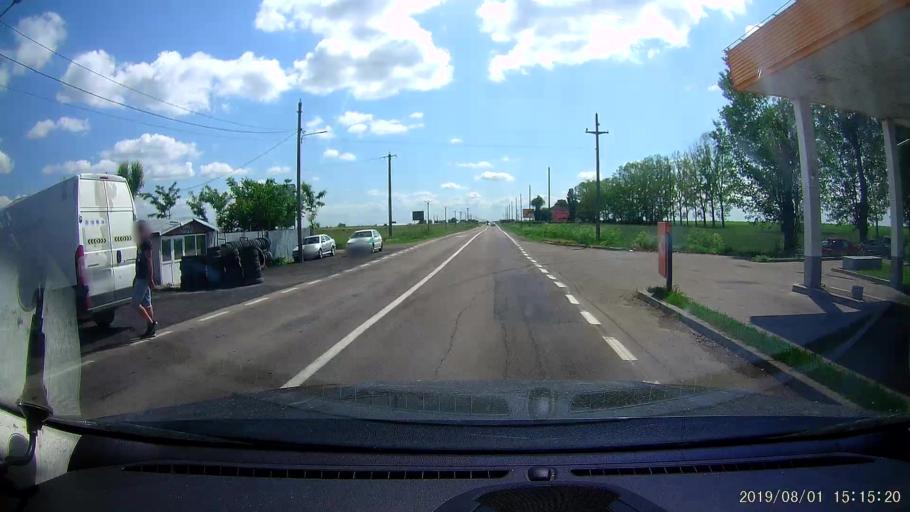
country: RO
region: Braila
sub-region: Comuna Chiscani
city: Lacu Sarat
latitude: 45.1655
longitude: 27.8694
